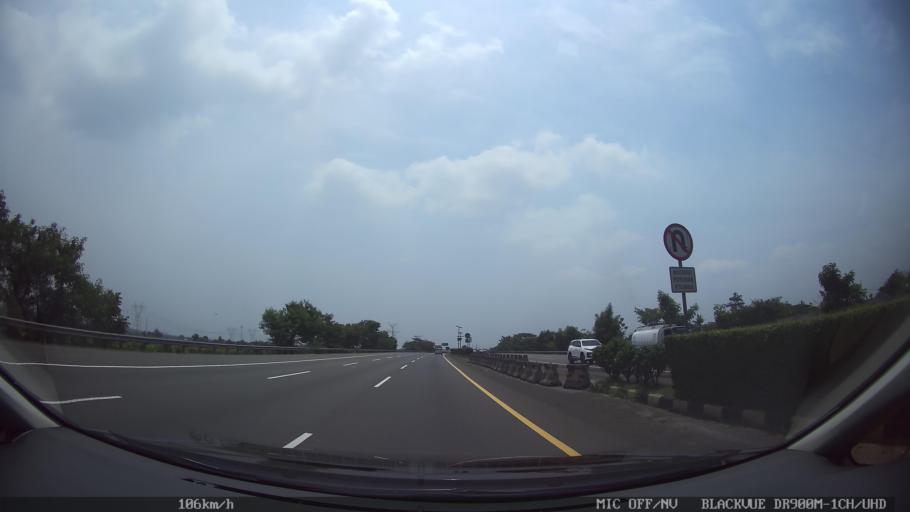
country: ID
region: West Java
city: Kresek
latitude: -6.1768
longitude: 106.3568
